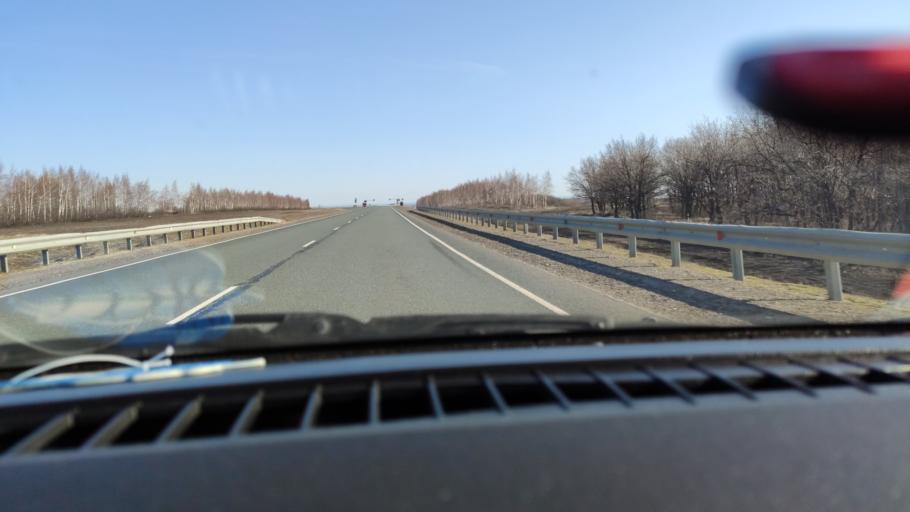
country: RU
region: Samara
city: Syzran'
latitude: 52.9489
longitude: 48.3050
